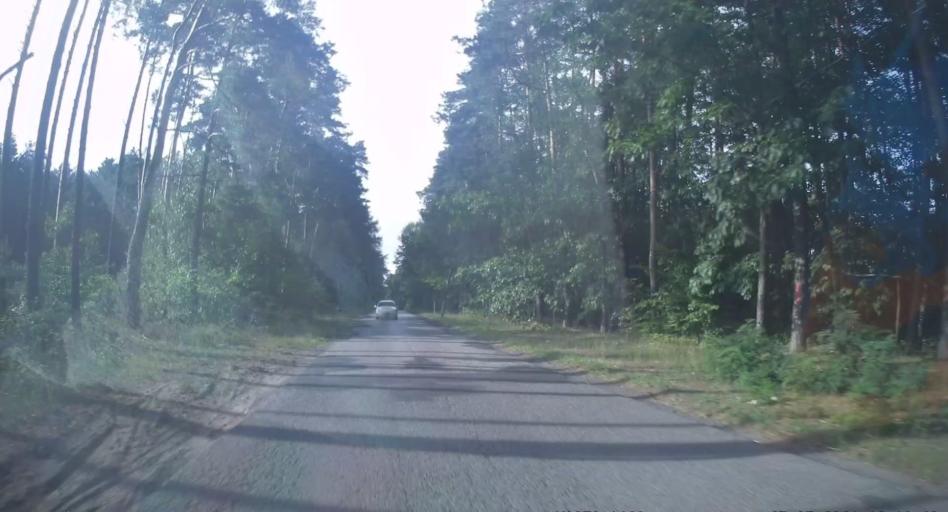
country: PL
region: Swietokrzyskie
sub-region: Powiat konecki
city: Konskie
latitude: 51.2238
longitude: 20.3863
